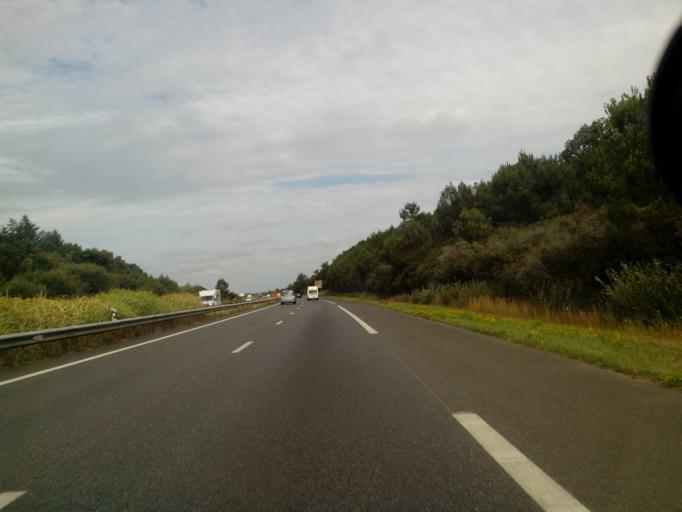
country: FR
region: Pays de la Loire
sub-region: Departement de la Loire-Atlantique
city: La Chapelle-des-Marais
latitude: 47.4957
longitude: -2.2485
